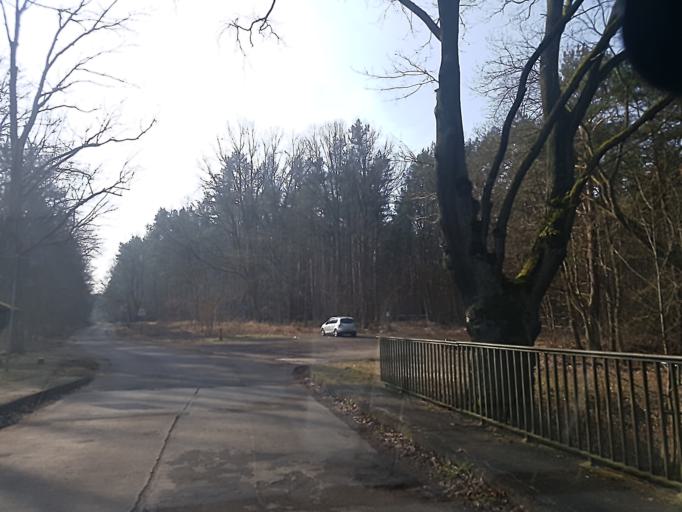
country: DE
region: Brandenburg
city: Wenzlow
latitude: 52.3591
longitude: 12.4684
